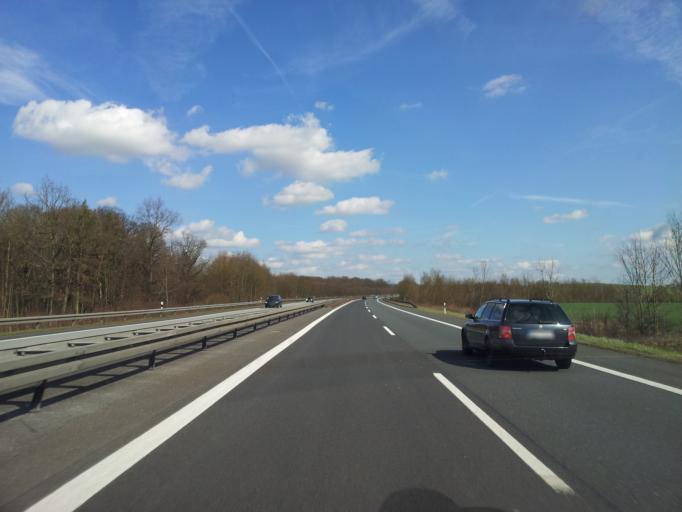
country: DE
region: Bavaria
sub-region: Regierungsbezirk Unterfranken
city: Wonfurt
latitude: 50.0060
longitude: 10.4844
